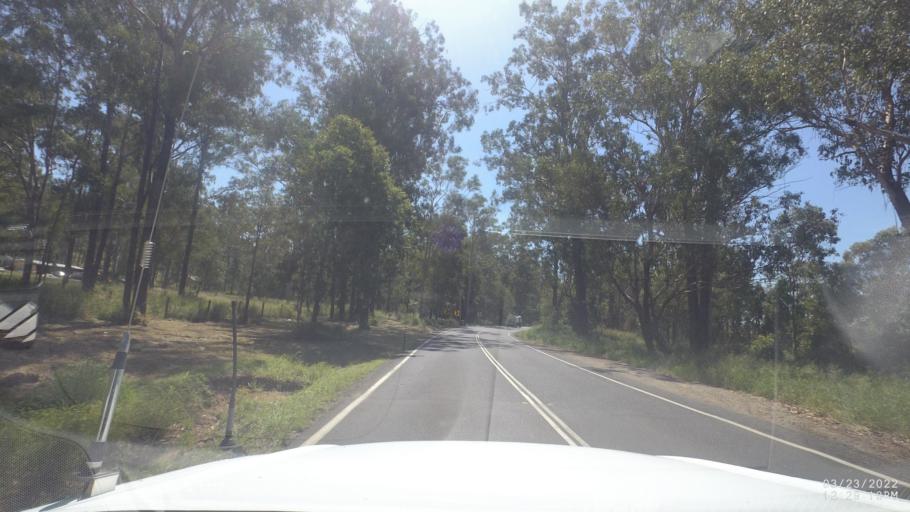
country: AU
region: Queensland
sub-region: Logan
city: Chambers Flat
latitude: -27.8070
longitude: 153.0974
